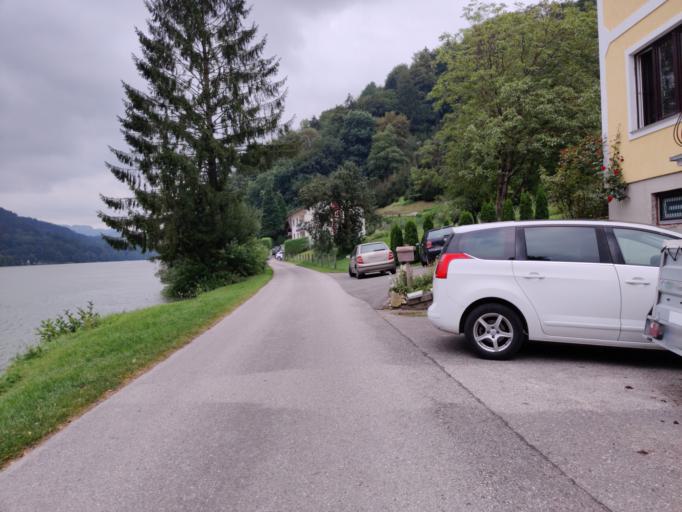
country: AT
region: Lower Austria
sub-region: Politischer Bezirk Melk
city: Nochling
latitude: 48.2199
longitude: 14.9473
